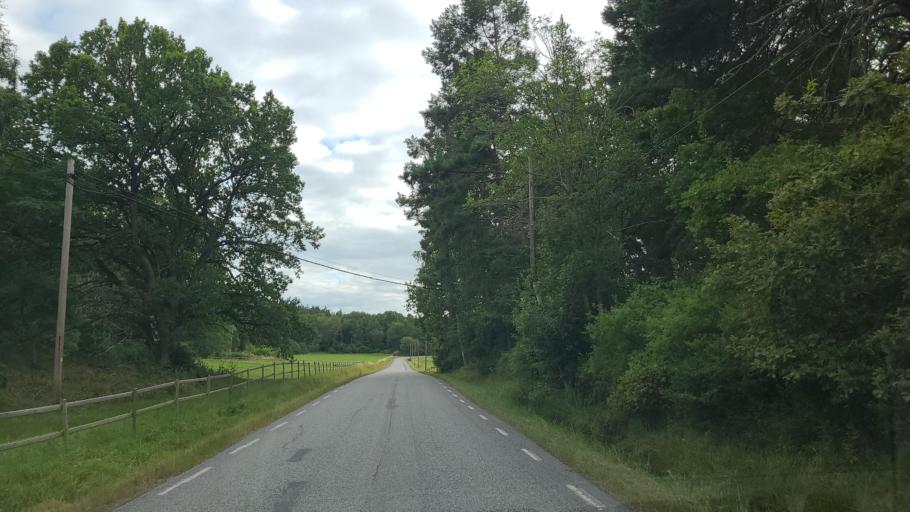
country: SE
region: Stockholm
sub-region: Upplands-Bro Kommun
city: Bro
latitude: 59.4750
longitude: 17.5961
